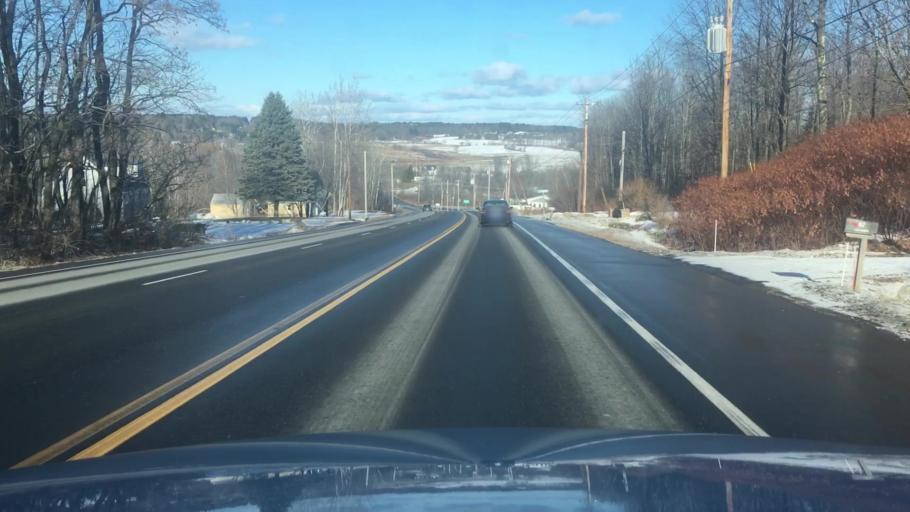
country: US
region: Maine
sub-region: Kennebec County
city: Waterville
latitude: 44.5949
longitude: -69.6538
